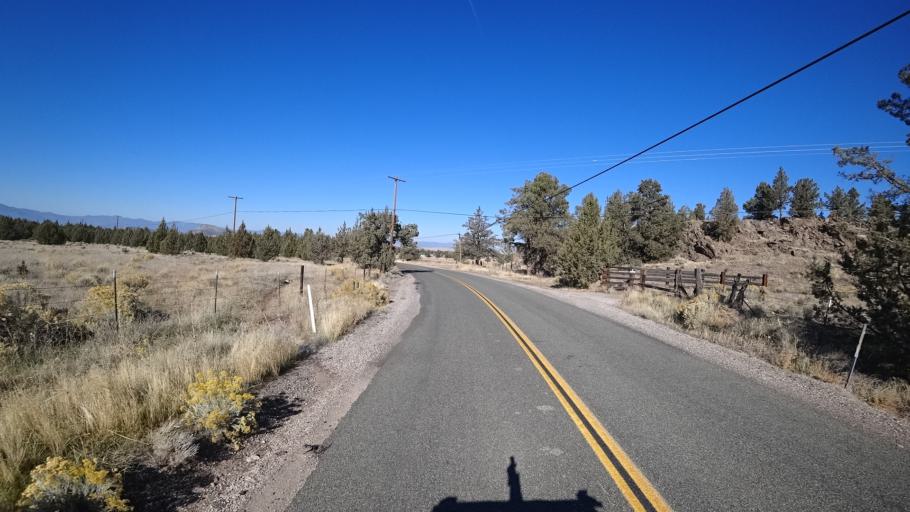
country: US
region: California
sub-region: Siskiyou County
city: Montague
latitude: 41.6396
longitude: -122.3418
